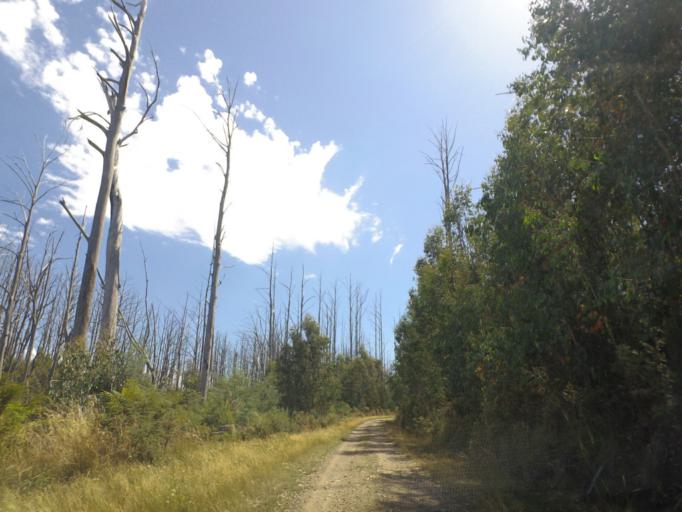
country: AU
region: Victoria
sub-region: Murrindindi
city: Alexandra
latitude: -37.4730
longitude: 145.8363
